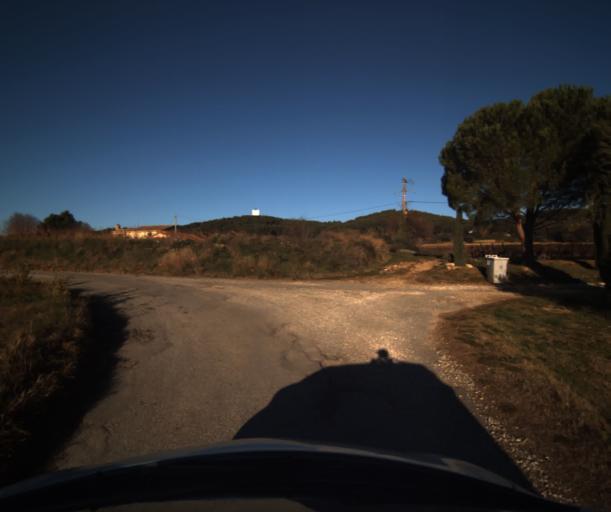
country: FR
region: Provence-Alpes-Cote d'Azur
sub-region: Departement du Vaucluse
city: Pertuis
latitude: 43.7075
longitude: 5.4883
